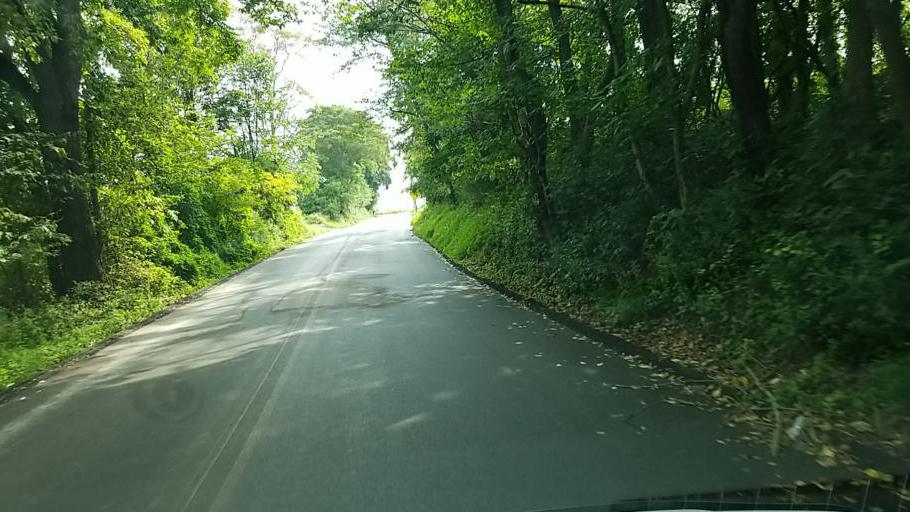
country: US
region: Pennsylvania
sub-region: Dauphin County
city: Matamoras
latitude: 40.4857
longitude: -76.9268
